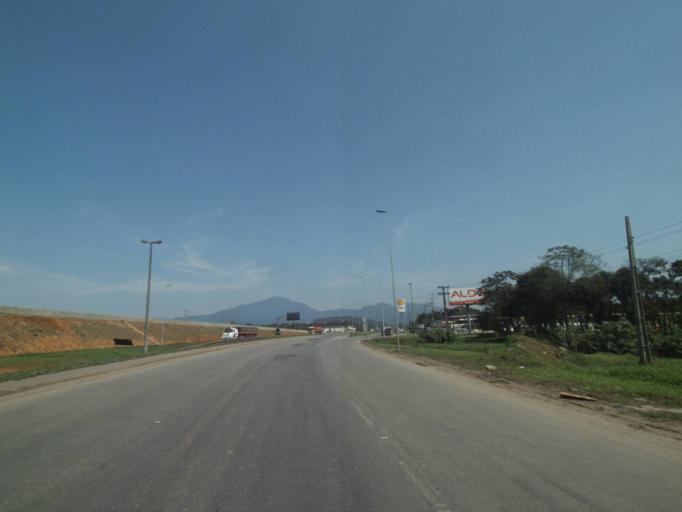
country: BR
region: Parana
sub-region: Paranagua
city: Paranagua
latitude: -25.5564
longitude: -48.5657
